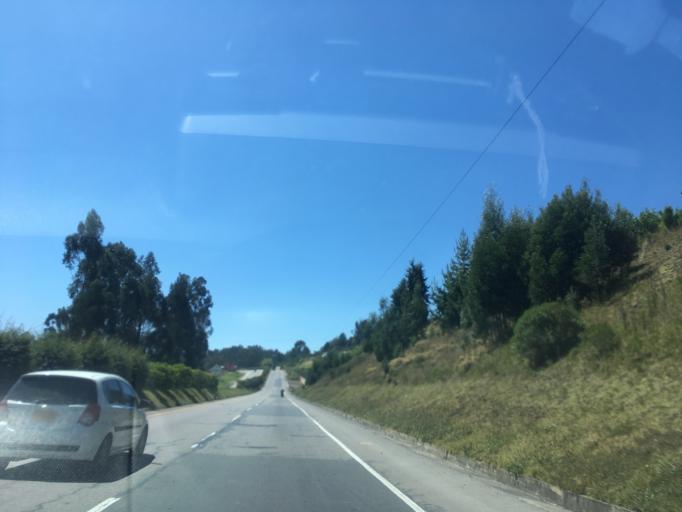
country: CO
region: Boyaca
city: Tuta
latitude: 5.6863
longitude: -73.2654
